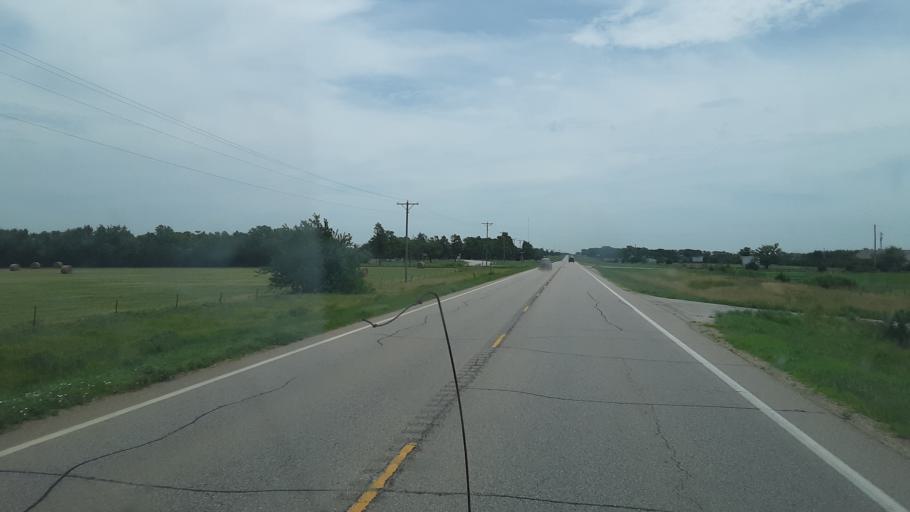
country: US
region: Kansas
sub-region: Butler County
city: El Dorado
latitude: 37.8105
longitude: -96.6637
